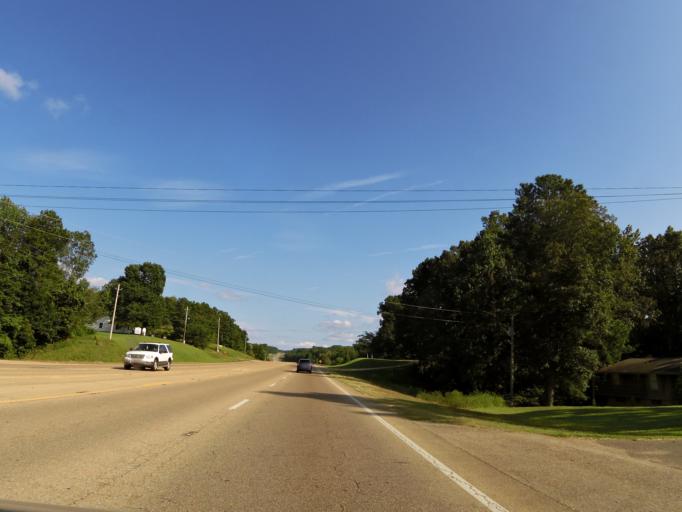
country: US
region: Mississippi
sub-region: Alcorn County
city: Farmington
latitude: 34.8962
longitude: -88.4703
